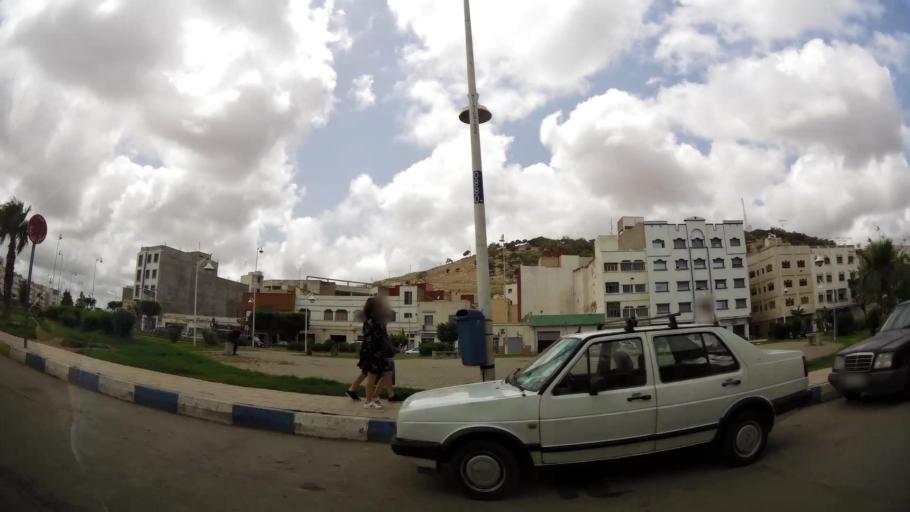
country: MA
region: Oriental
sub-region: Nador
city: Nador
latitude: 35.1802
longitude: -2.9279
